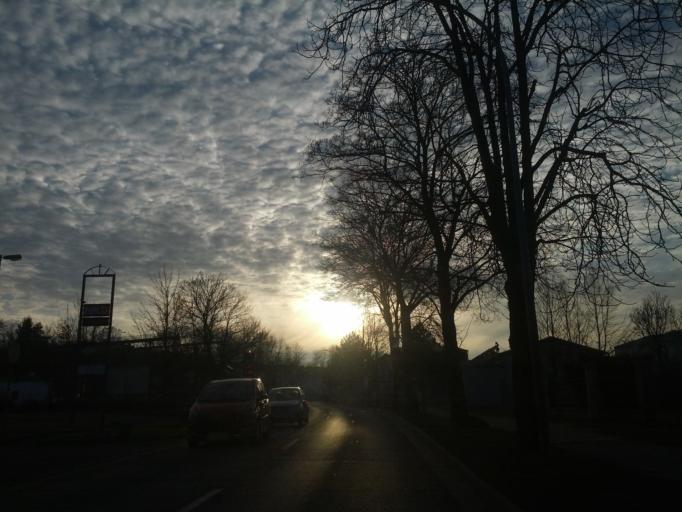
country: DE
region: Thuringia
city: Bad Langensalza
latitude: 51.1036
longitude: 10.6383
